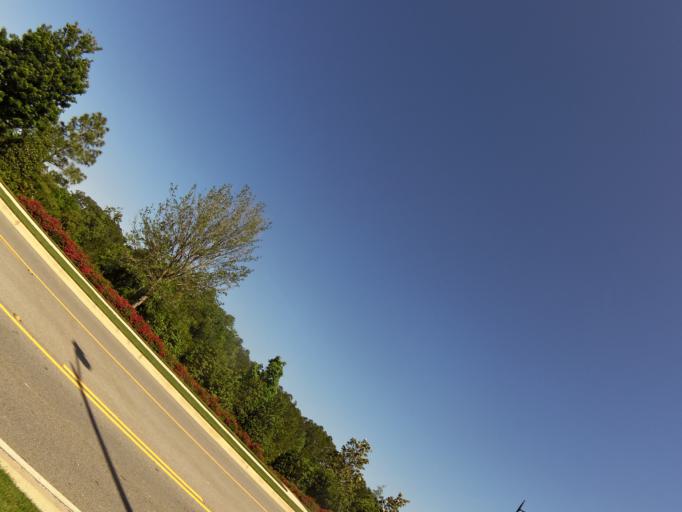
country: US
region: Georgia
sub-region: Columbia County
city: Martinez
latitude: 33.5057
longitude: -82.0316
